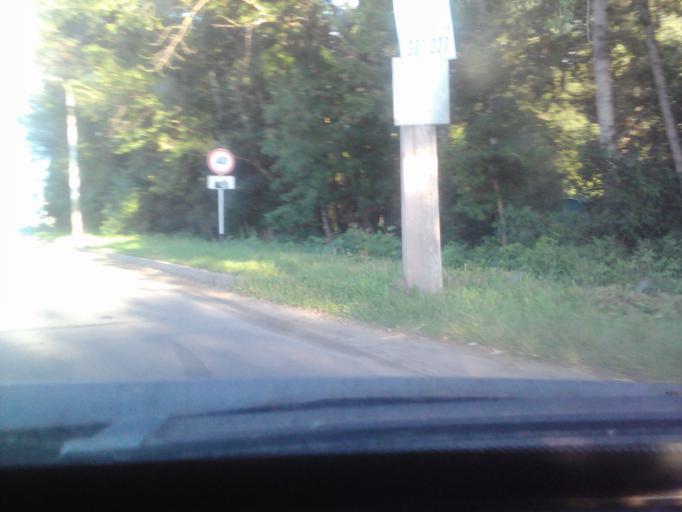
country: RU
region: Kursk
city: Kurchatov
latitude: 51.6589
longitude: 35.6444
